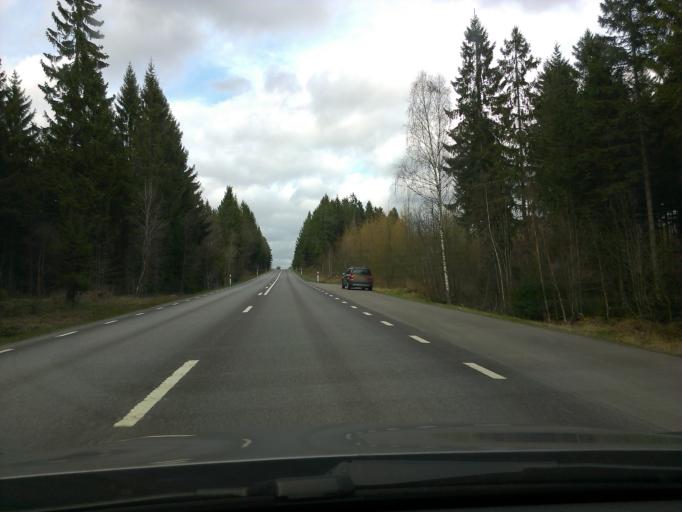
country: SE
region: Kronoberg
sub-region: Vaxjo Kommun
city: Gemla
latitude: 56.7865
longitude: 14.6124
